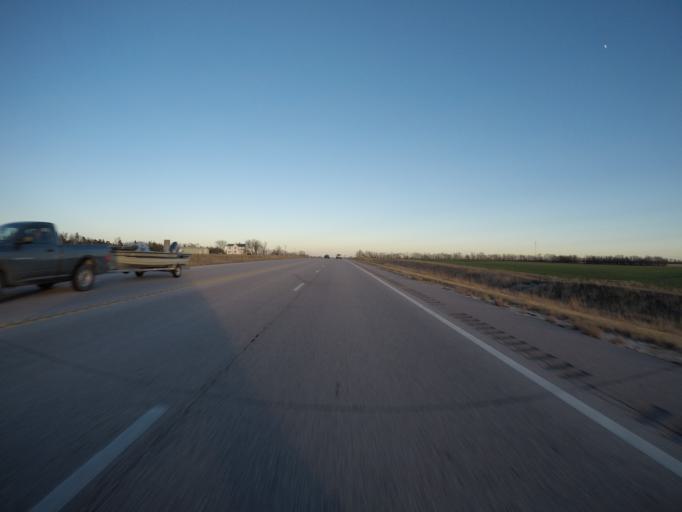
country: US
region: Kansas
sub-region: Marion County
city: Peabody
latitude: 38.1746
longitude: -97.1491
